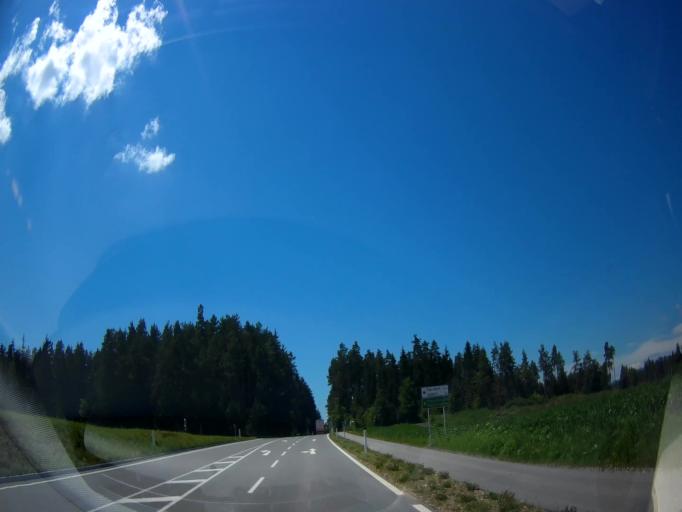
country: AT
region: Carinthia
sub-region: Politischer Bezirk Volkermarkt
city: Eberndorf
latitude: 46.6121
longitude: 14.6718
